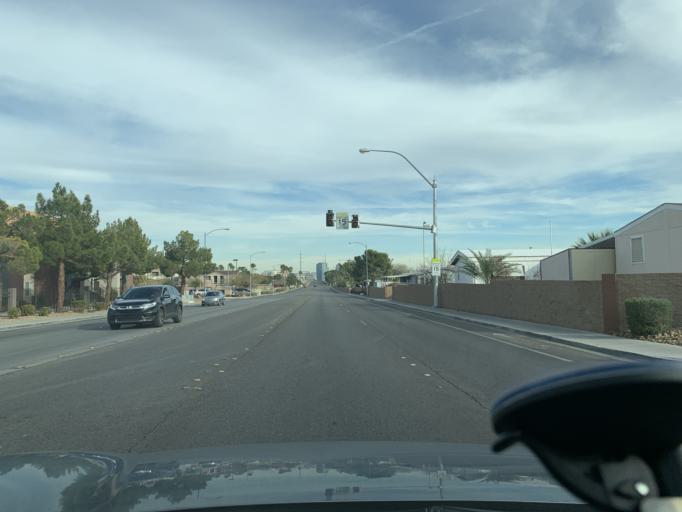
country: US
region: Nevada
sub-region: Clark County
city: Spring Valley
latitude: 36.1073
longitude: -115.2216
